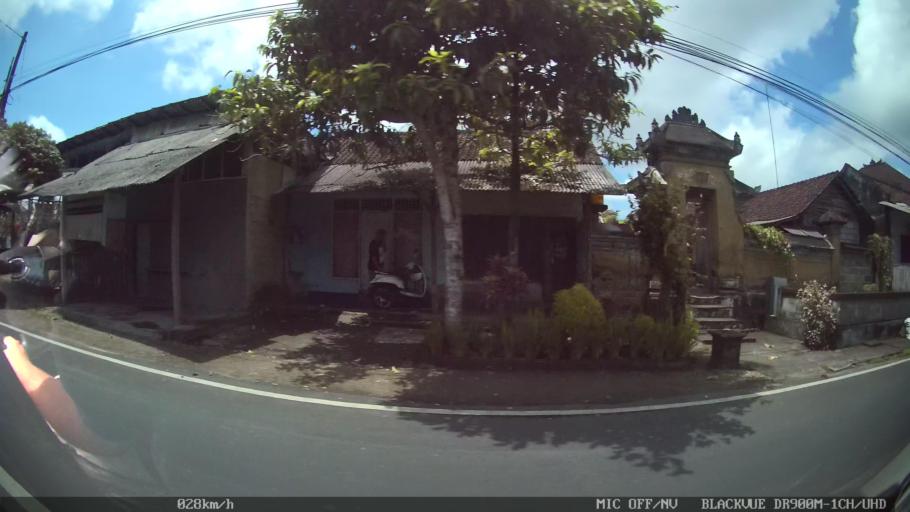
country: ID
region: Bali
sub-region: Kabupaten Gianyar
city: Ubud
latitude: -8.5253
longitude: 115.2839
